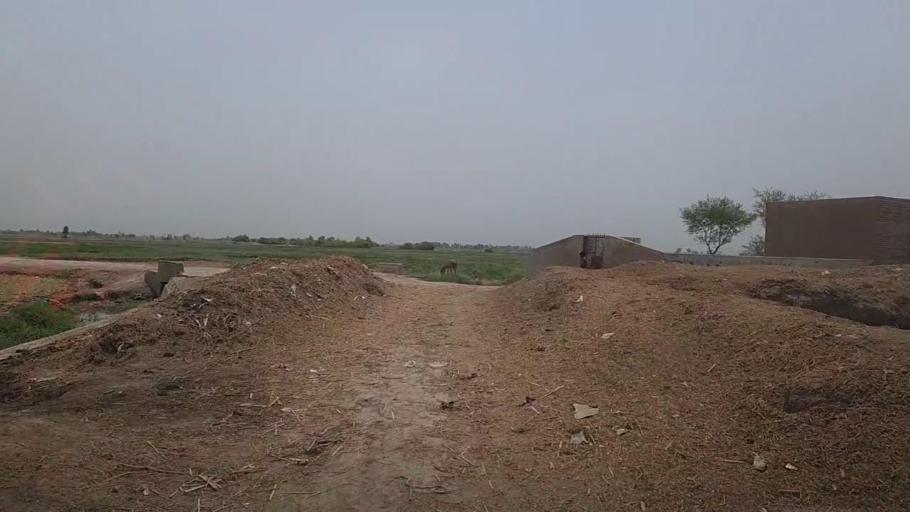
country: PK
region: Sindh
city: Sita Road
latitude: 27.0708
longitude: 67.8516
